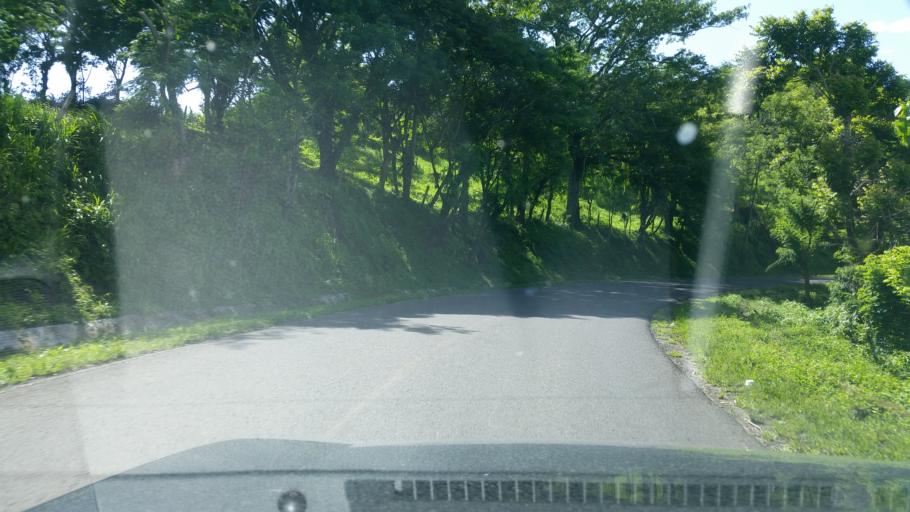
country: NI
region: Matagalpa
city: San Ramon
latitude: 13.0078
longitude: -85.7969
